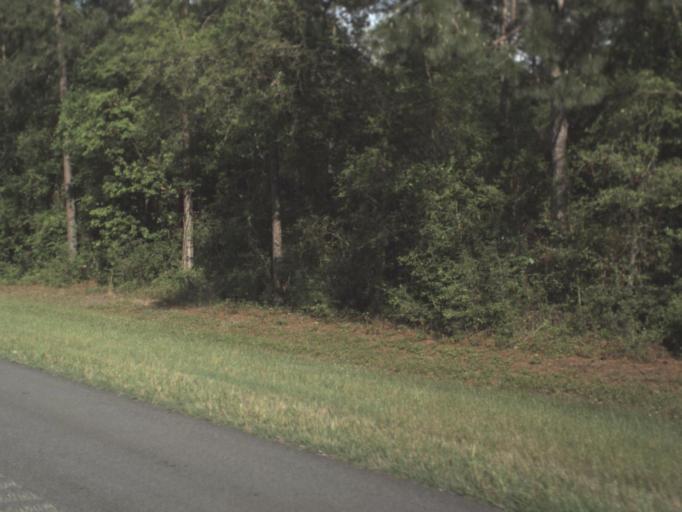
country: US
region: Florida
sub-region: Holmes County
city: Bonifay
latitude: 30.7453
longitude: -85.8699
